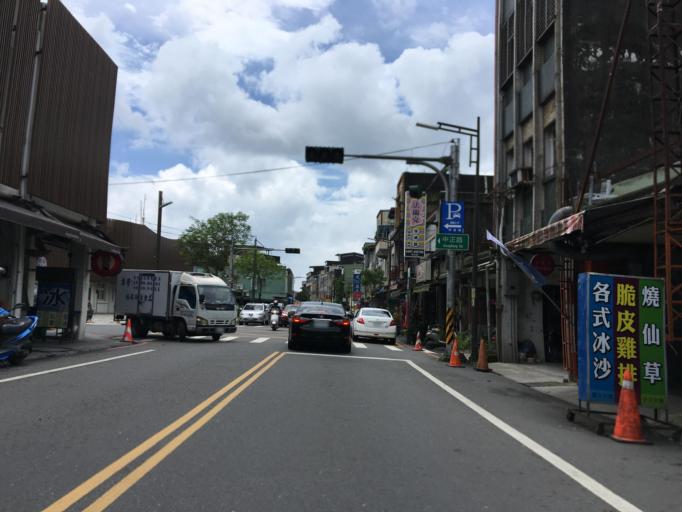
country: TW
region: Taiwan
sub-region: Yilan
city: Yilan
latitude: 24.6348
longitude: 121.7899
